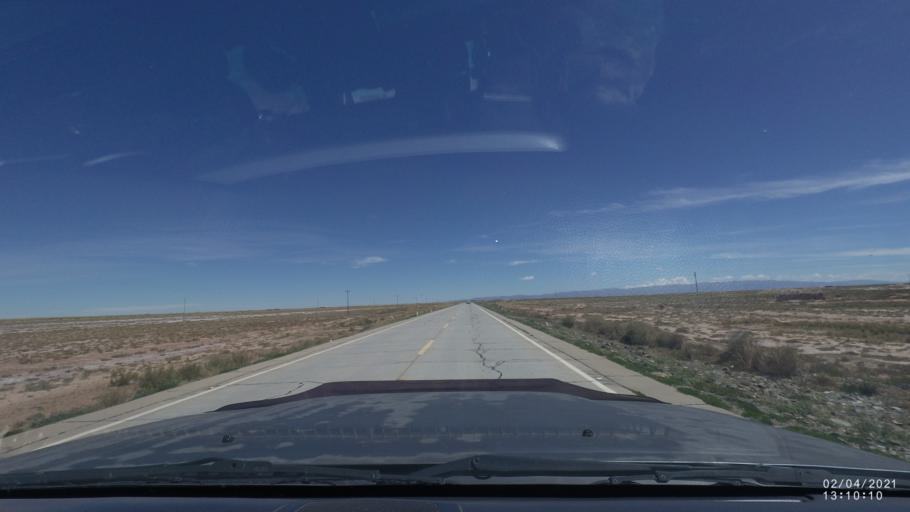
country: BO
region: Oruro
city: Oruro
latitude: -18.0900
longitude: -67.2576
